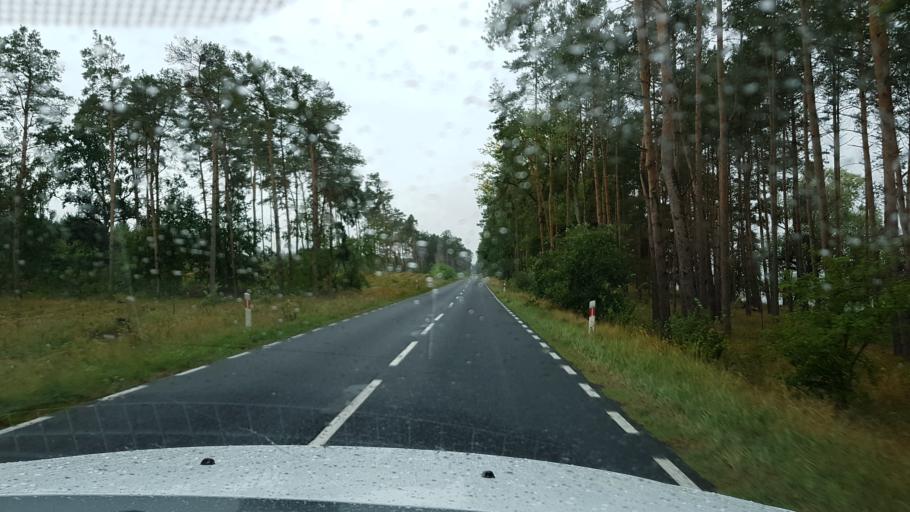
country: DE
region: Brandenburg
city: Schwedt (Oder)
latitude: 53.0481
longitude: 14.3420
